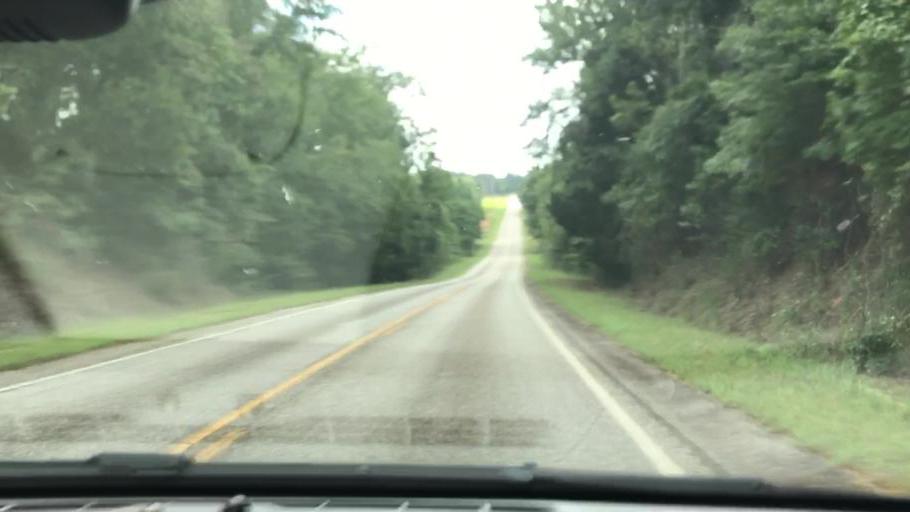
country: US
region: Georgia
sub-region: Stewart County
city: Lumpkin
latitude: 32.0578
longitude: -84.8137
